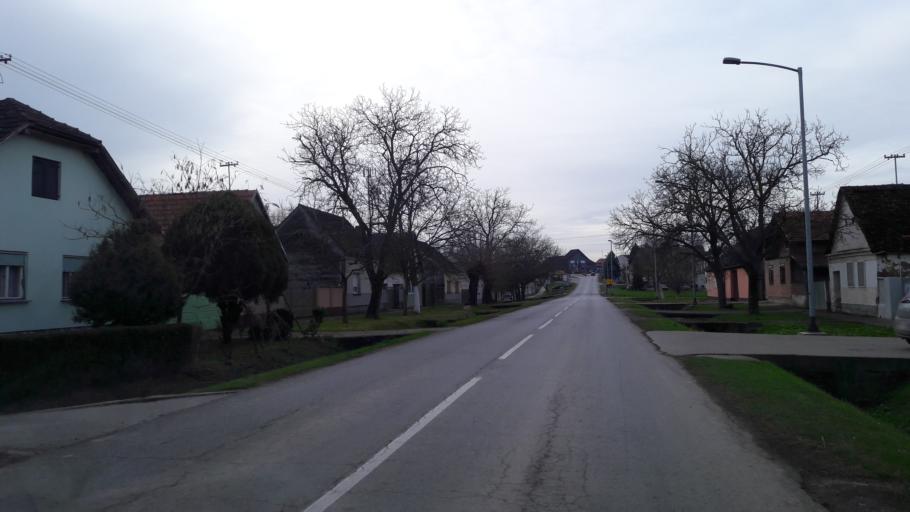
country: HR
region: Osjecko-Baranjska
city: Semeljci
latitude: 45.3630
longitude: 18.5440
